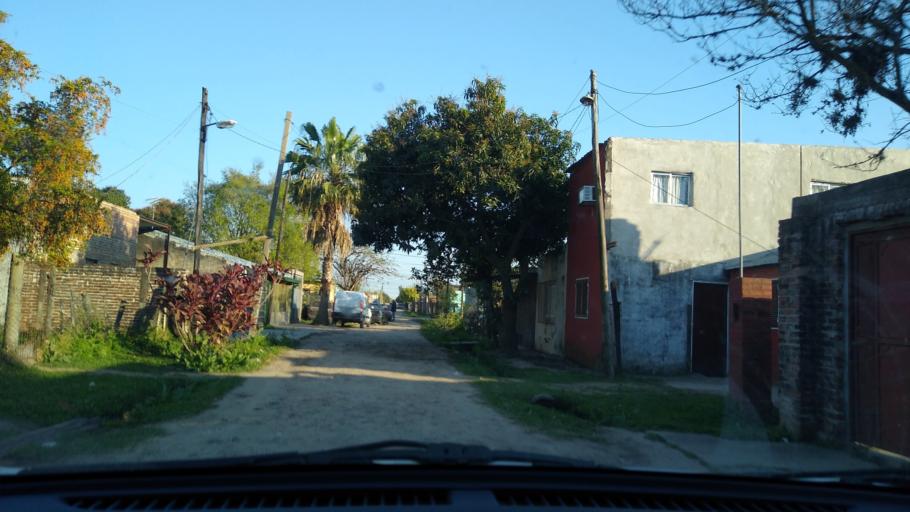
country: AR
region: Chaco
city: Resistencia
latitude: -27.4848
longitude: -58.9691
